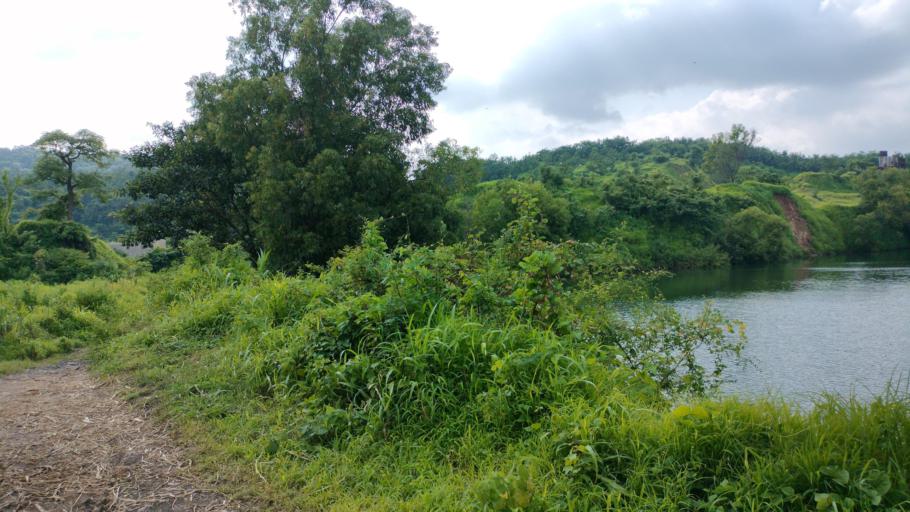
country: IN
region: Maharashtra
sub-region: Thane
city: Virar
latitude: 19.4635
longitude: 72.8802
